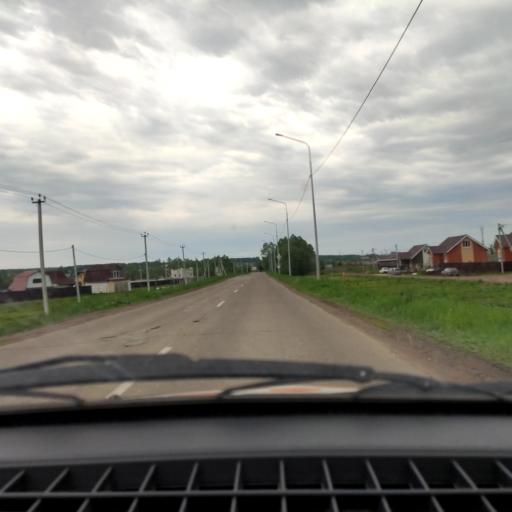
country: RU
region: Bashkortostan
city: Avdon
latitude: 54.5539
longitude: 55.7583
